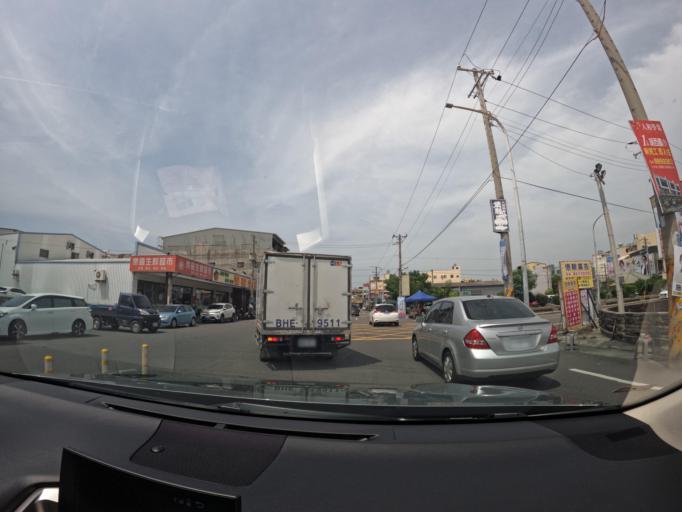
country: TW
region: Taiwan
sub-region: Changhua
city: Chang-hua
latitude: 23.9614
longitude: 120.4773
